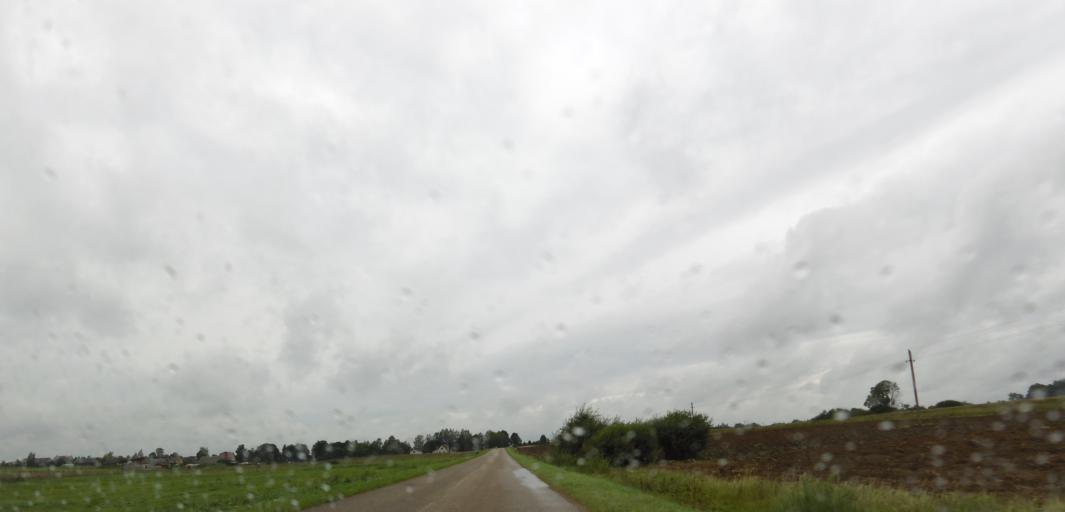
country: LT
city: Sirvintos
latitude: 55.0834
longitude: 25.0020
